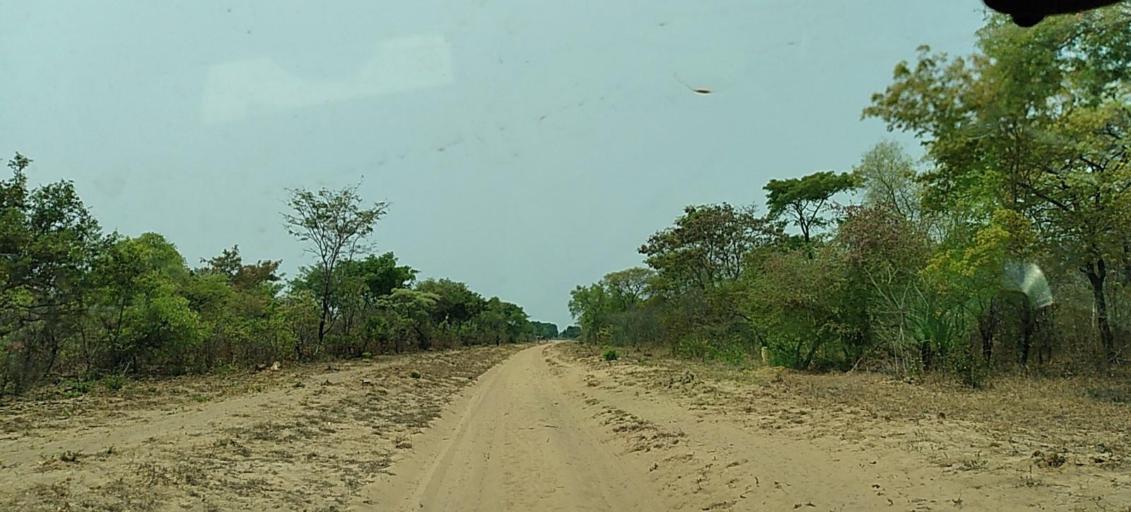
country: ZM
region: Western
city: Lukulu
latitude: -14.1531
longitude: 23.3014
